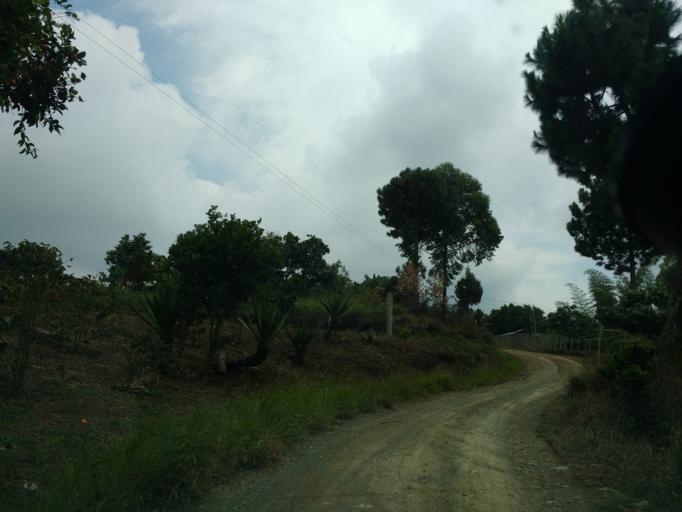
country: CO
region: Cauca
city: Santander de Quilichao
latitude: 2.9152
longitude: -76.4764
